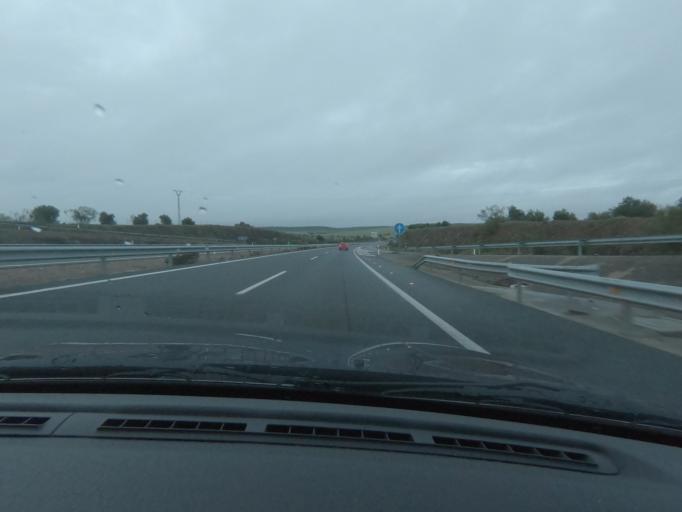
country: ES
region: Extremadura
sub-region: Provincia de Badajoz
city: Aljucen
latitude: 39.0415
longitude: -6.3388
